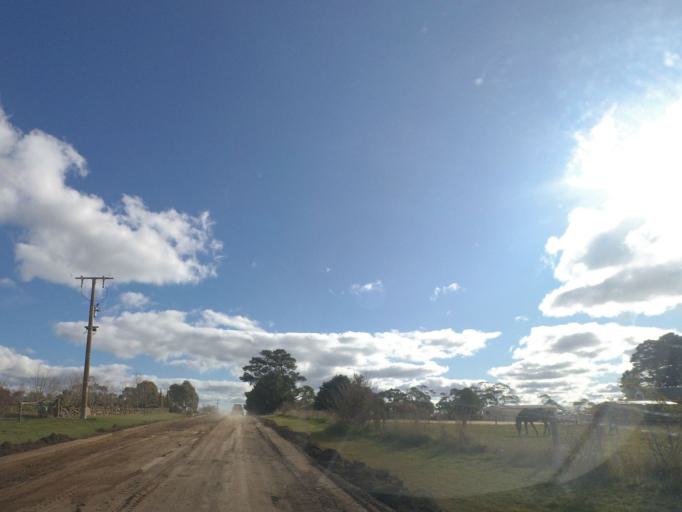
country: AU
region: Victoria
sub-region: Mount Alexander
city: Castlemaine
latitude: -37.2552
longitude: 144.4349
